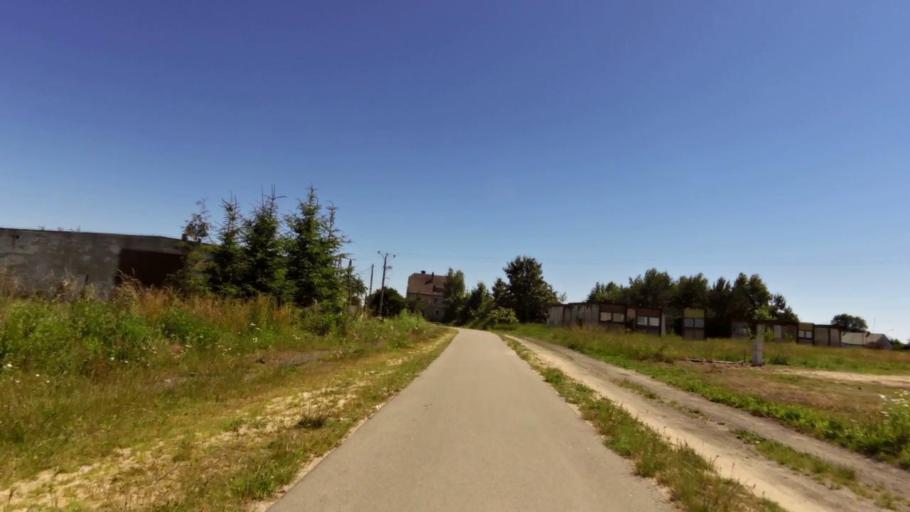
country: PL
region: West Pomeranian Voivodeship
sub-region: Powiat kolobrzeski
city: Kolobrzeg
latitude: 54.0926
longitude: 15.5732
